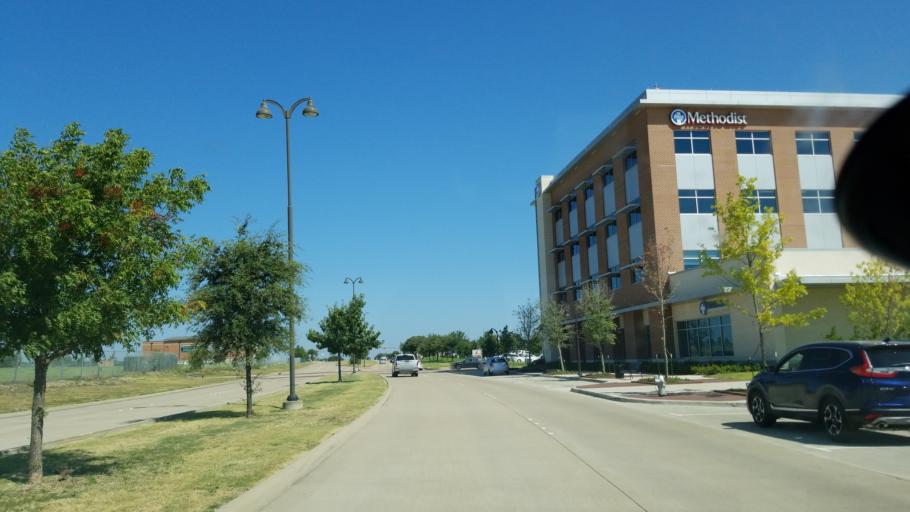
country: US
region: Texas
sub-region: Tarrant County
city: Mansfield
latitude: 32.5655
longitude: -97.0954
